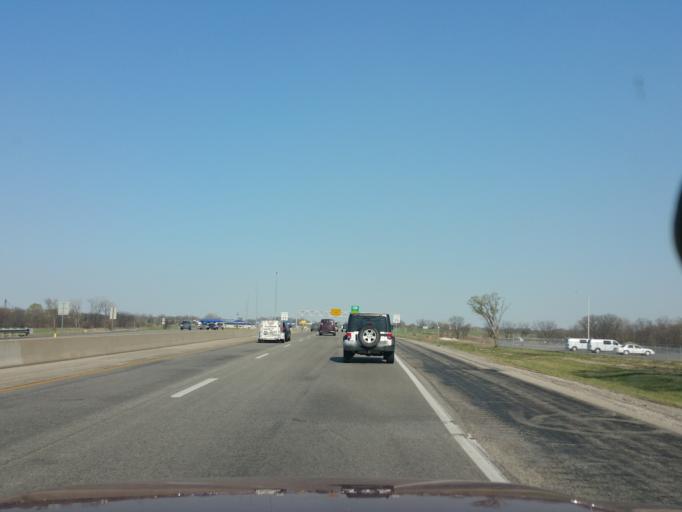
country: US
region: Kansas
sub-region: Leavenworth County
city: Tonganoxie
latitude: 39.0687
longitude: -95.0153
